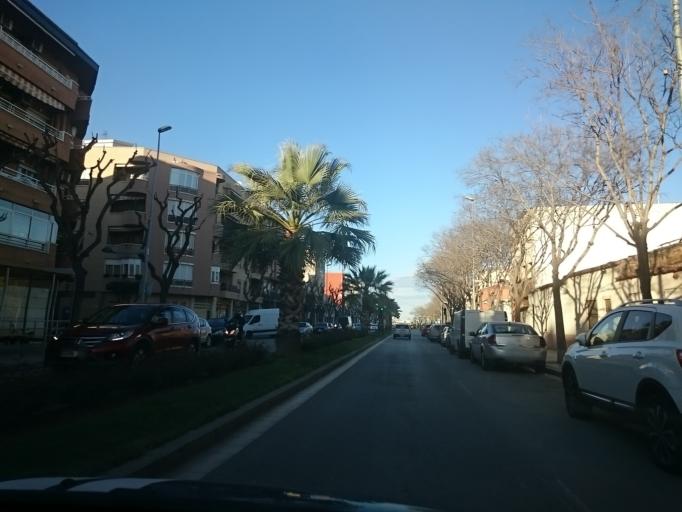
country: ES
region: Catalonia
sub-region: Provincia de Barcelona
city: El Prat de Llobregat
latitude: 41.3207
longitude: 2.0993
